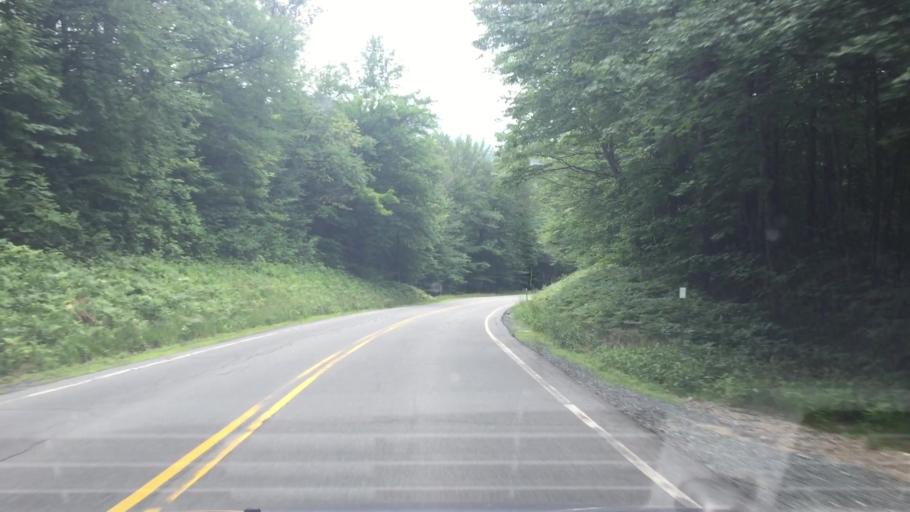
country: US
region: New Hampshire
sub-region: Grafton County
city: Deerfield
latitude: 44.2053
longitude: -71.6844
